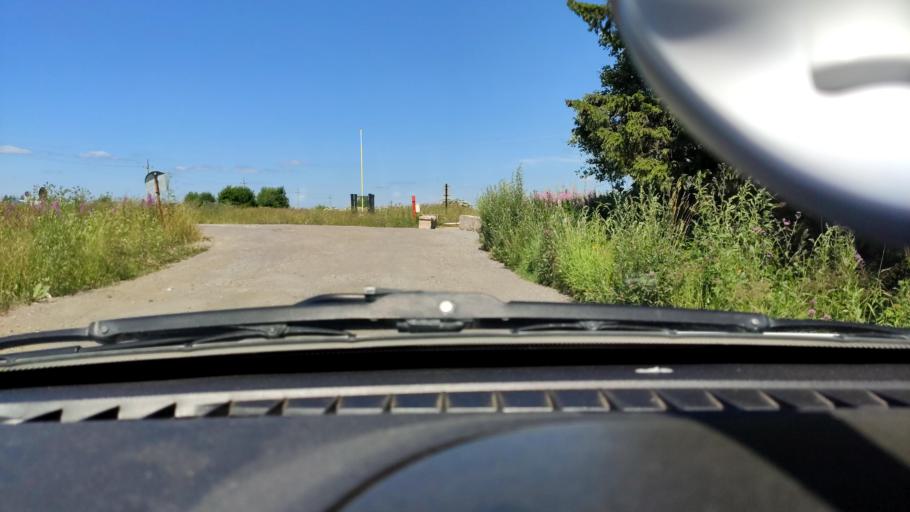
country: RU
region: Perm
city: Polazna
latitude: 58.1995
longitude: 56.4044
